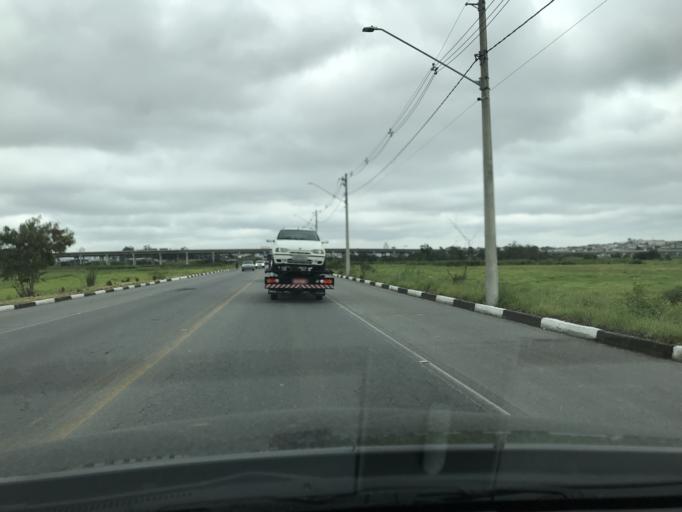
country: BR
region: Sao Paulo
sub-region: Itaquaquecetuba
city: Itaquaquecetuba
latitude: -23.5041
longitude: -46.3242
